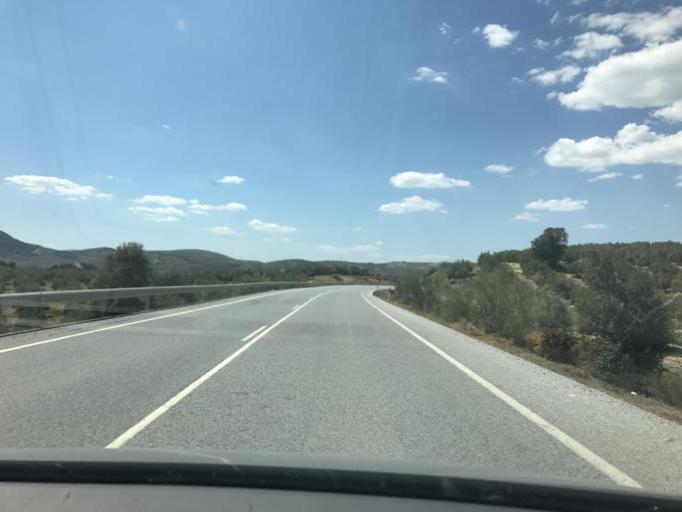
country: ES
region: Andalusia
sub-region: Provincia de Granada
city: Benalua de las Villas
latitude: 37.4261
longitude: -3.7117
